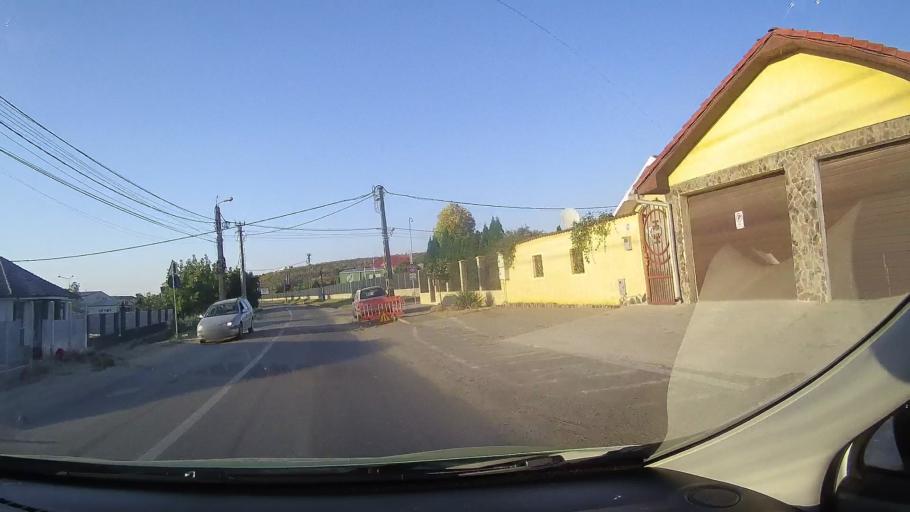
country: RO
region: Bihor
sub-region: Comuna Biharea
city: Oradea
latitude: 47.0926
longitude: 21.9256
